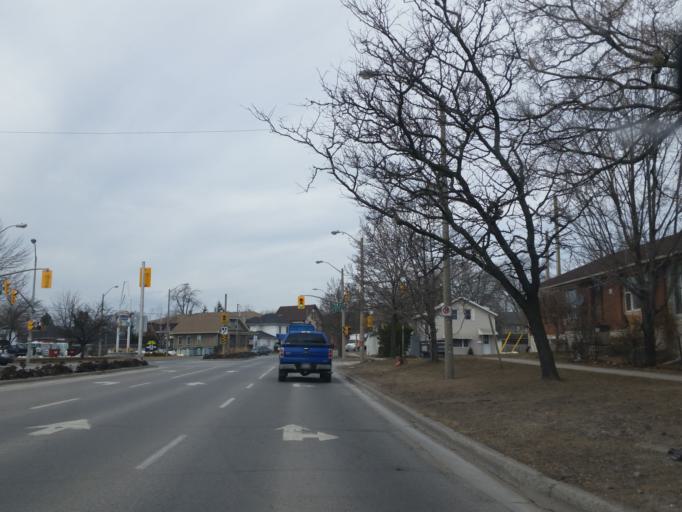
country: CA
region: Ontario
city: Belleville
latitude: 44.1708
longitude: -77.3864
